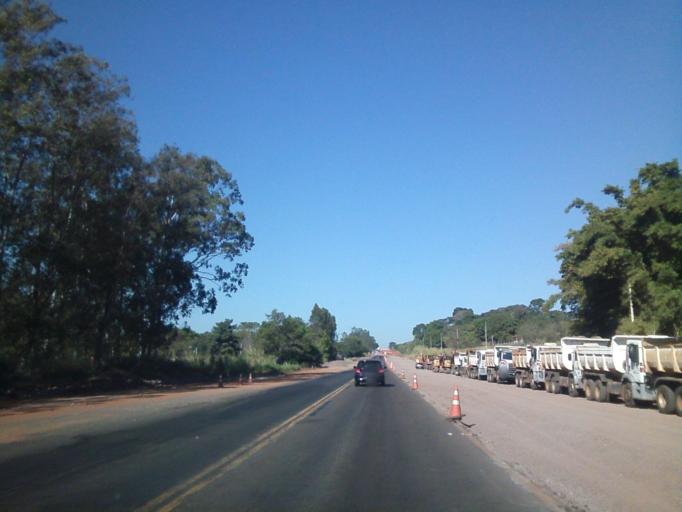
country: BR
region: Sao Paulo
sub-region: Pirapozinho
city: Pirapozinho
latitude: -22.2168
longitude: -51.4383
